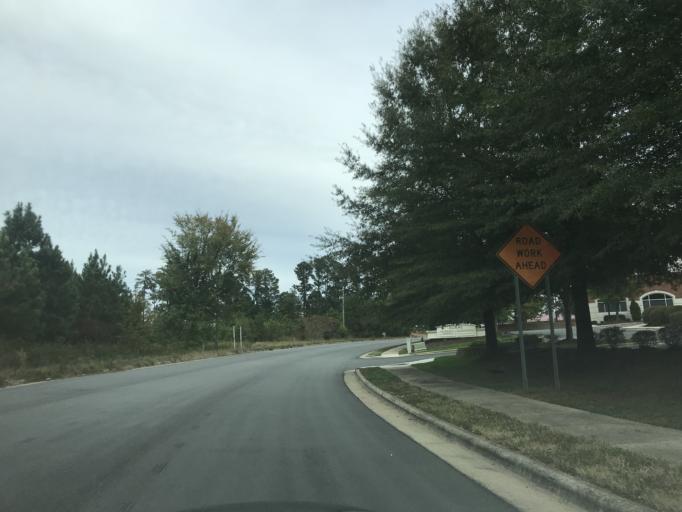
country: US
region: North Carolina
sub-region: Wake County
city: Wake Forest
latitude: 35.9535
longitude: -78.5424
